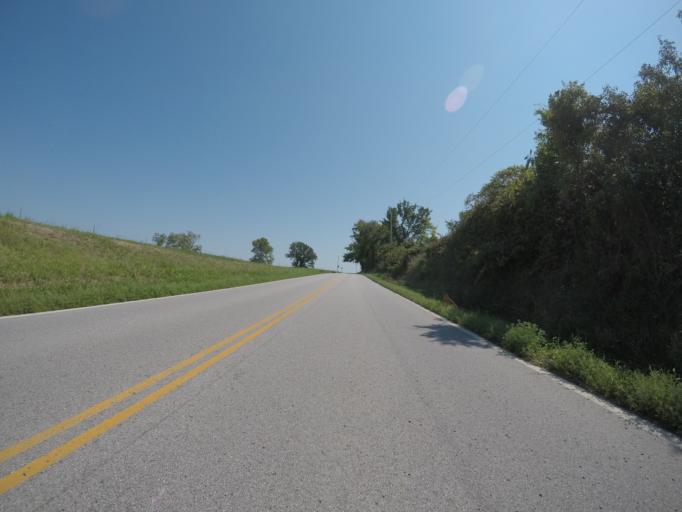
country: US
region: Kansas
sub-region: Leavenworth County
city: Lansing
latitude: 39.2347
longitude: -94.8641
